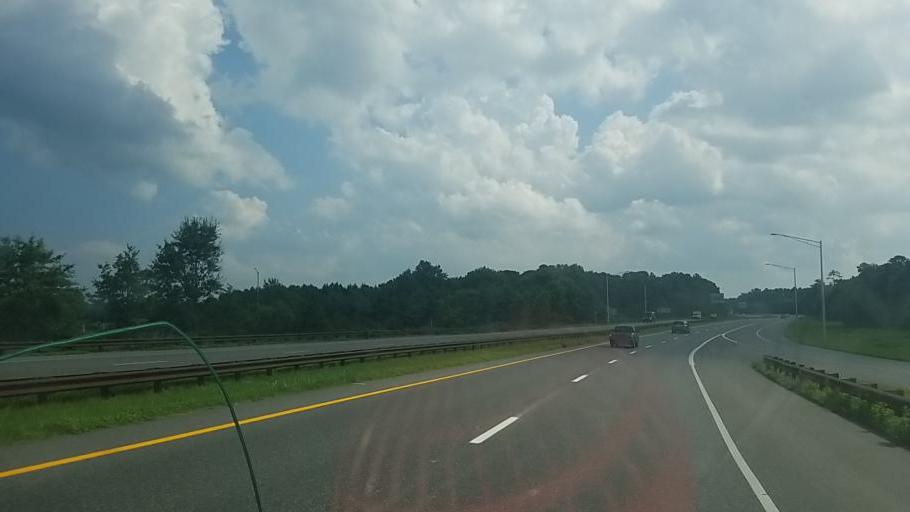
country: US
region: Maryland
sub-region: Worcester County
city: Ocean Pines
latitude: 38.3878
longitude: -75.2036
